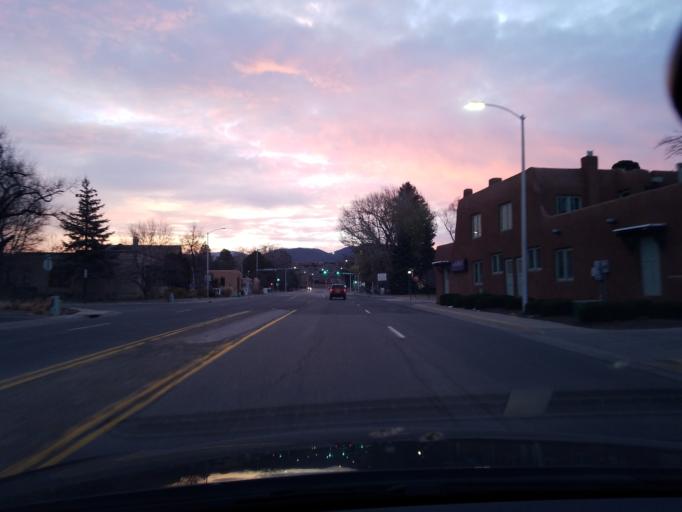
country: US
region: New Mexico
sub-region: Santa Fe County
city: Santa Fe
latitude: 35.6923
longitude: -105.9401
